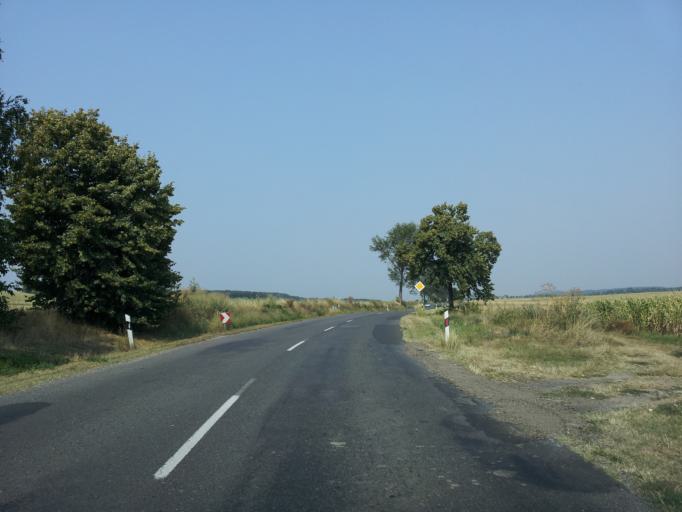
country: HU
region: Gyor-Moson-Sopron
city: Bakonyszentlaszlo
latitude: 47.4722
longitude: 17.7938
